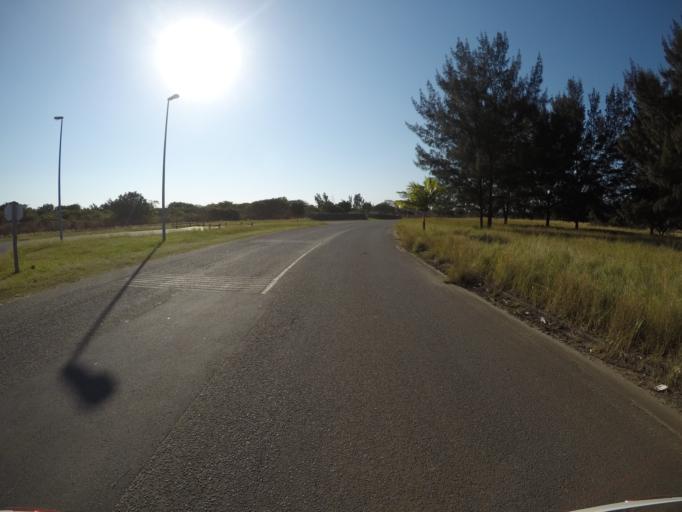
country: ZA
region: KwaZulu-Natal
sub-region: uThungulu District Municipality
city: Richards Bay
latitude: -28.7919
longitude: 32.0775
